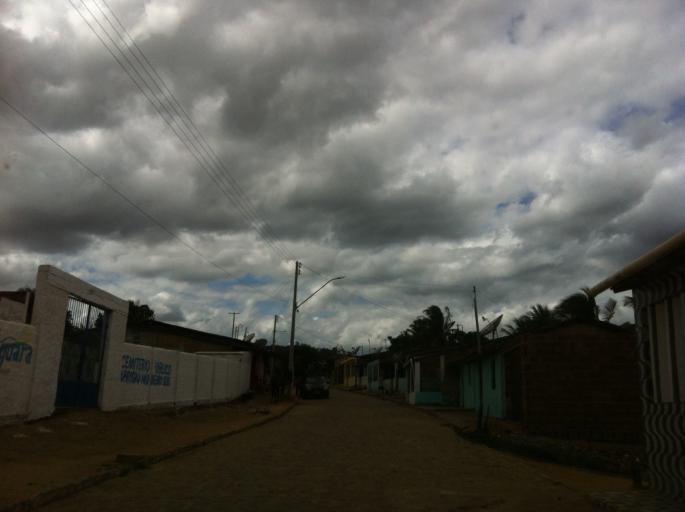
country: BR
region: Alagoas
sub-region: Ibateguara
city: Ibateguara
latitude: -8.9508
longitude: -35.9528
